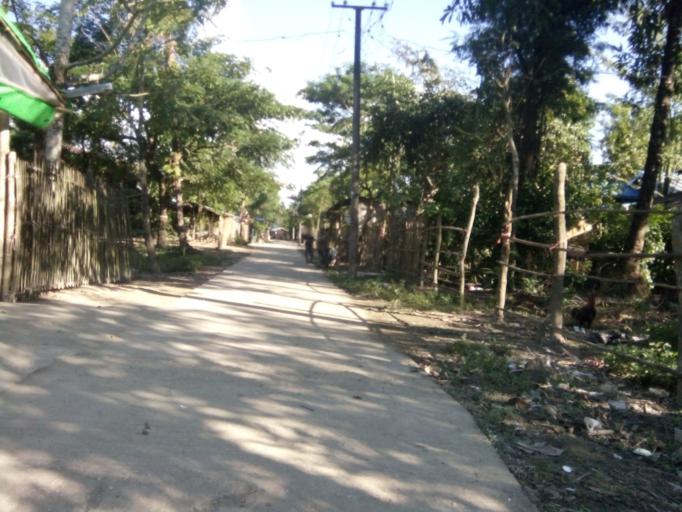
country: MM
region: Yangon
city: Kanbe
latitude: 16.8740
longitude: 95.9791
